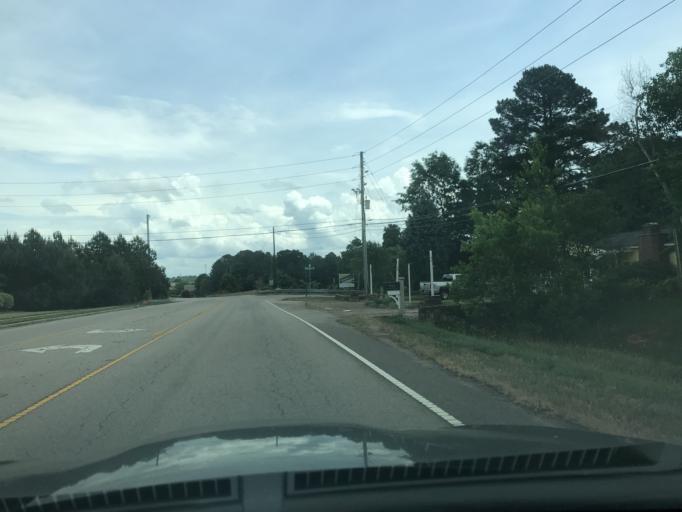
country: US
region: North Carolina
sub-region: Wake County
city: West Raleigh
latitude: 35.8844
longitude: -78.5928
